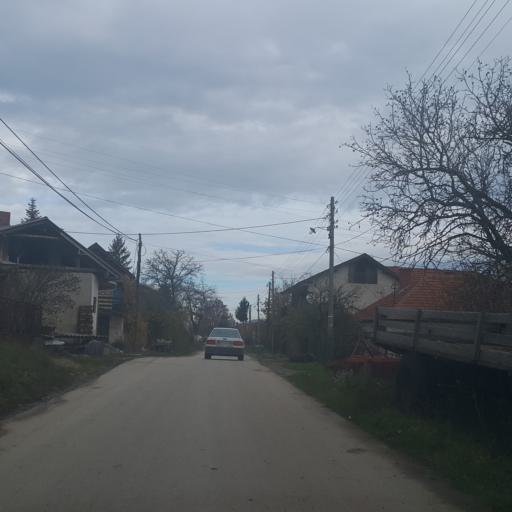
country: RS
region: Central Serbia
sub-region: Zajecarski Okrug
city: Knjazevac
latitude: 43.5962
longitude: 22.2549
